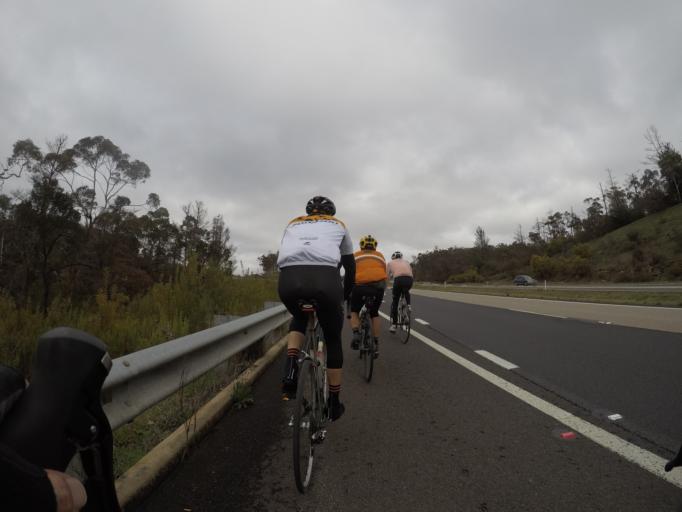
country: AU
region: New South Wales
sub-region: Lithgow
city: Lithgow
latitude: -33.4318
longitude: 150.0741
